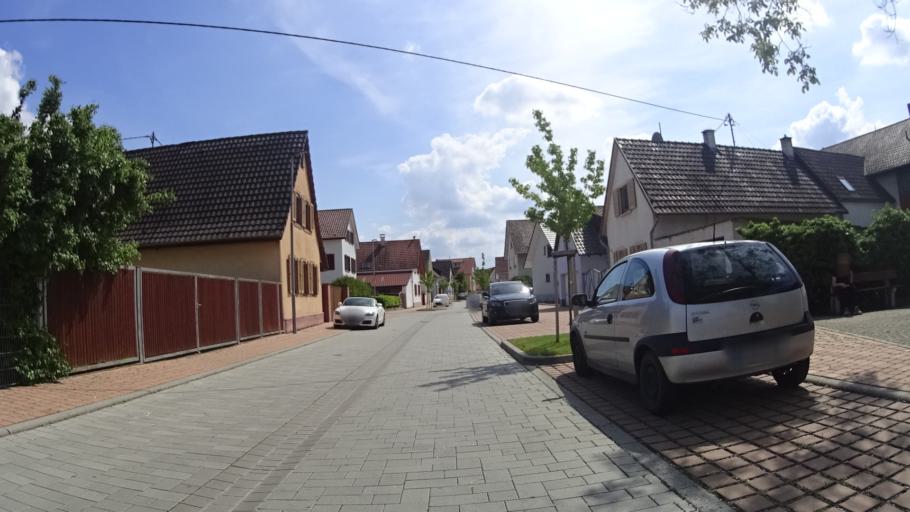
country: DE
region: Baden-Wuerttemberg
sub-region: Freiburg Region
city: Sasbach
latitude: 48.1419
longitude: 7.6165
